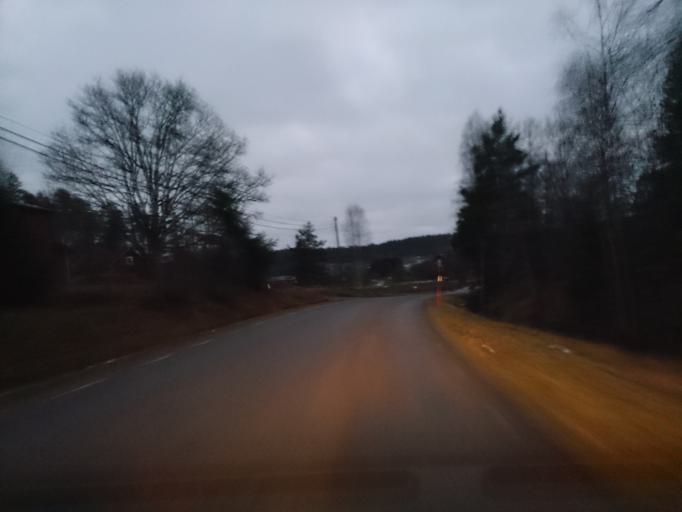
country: SE
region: OEstergoetland
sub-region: Atvidabergs Kommun
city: Atvidaberg
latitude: 58.2201
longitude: 16.0496
